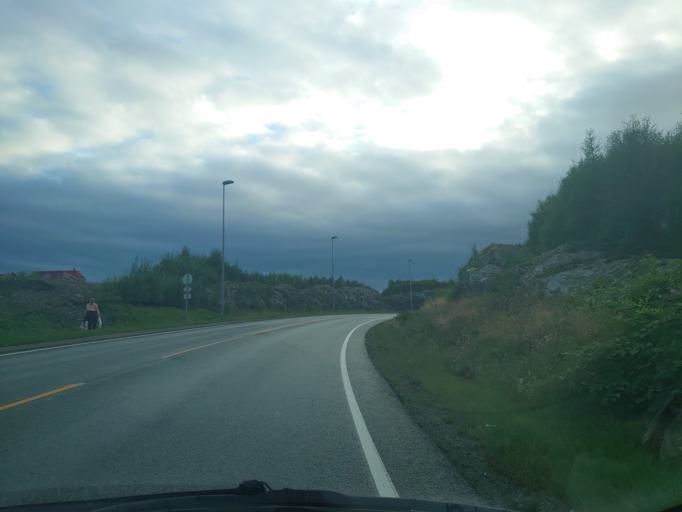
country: NO
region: Hordaland
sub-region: Lindas
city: Isdalsto
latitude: 60.5579
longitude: 5.2666
